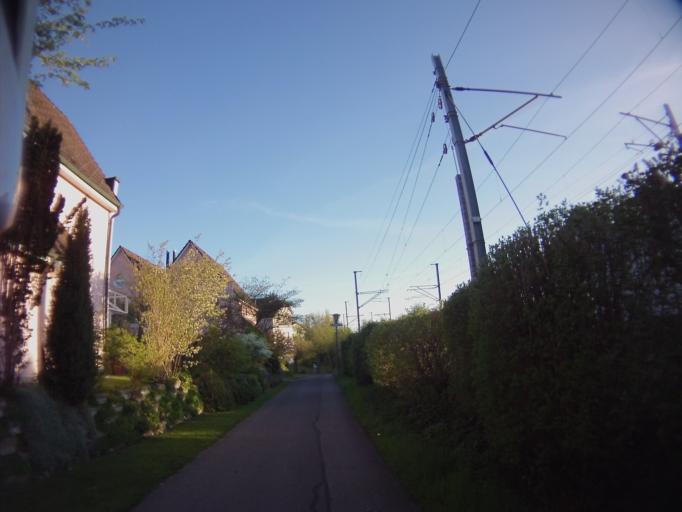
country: CH
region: Zurich
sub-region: Bezirk Affoltern
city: Affoltern / Unterdorf
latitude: 47.2825
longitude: 8.4516
